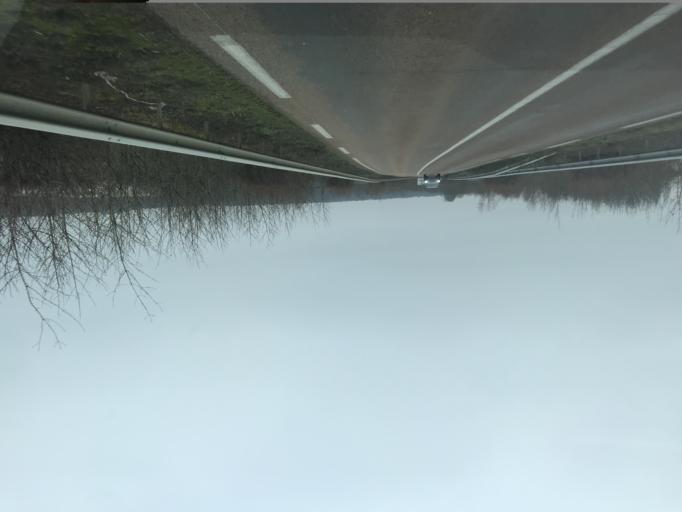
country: FR
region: Bourgogne
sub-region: Departement de l'Yonne
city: Avallon
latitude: 47.4981
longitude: 3.9324
